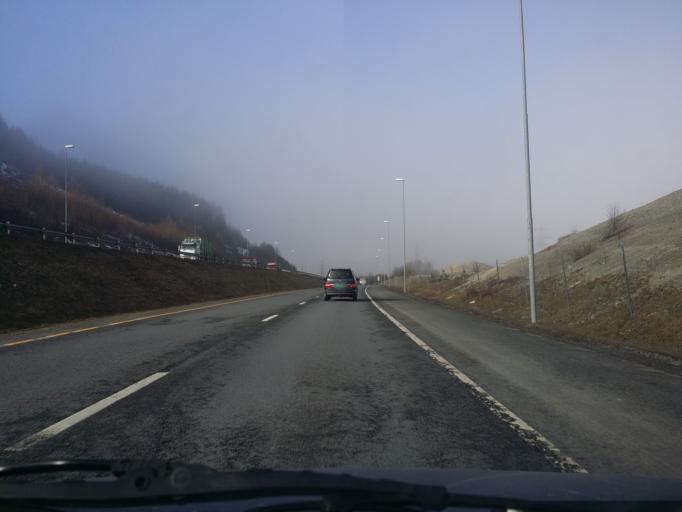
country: NO
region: Buskerud
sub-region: Nedre Eiker
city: Mjondalen
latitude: 59.7464
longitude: 10.0593
